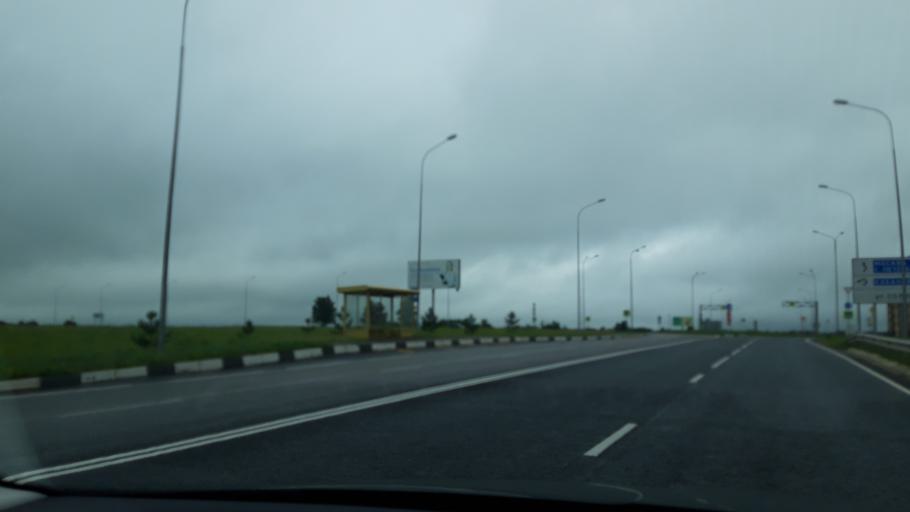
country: RU
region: Tverskaya
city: Zavidovo
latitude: 56.5787
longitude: 36.5216
